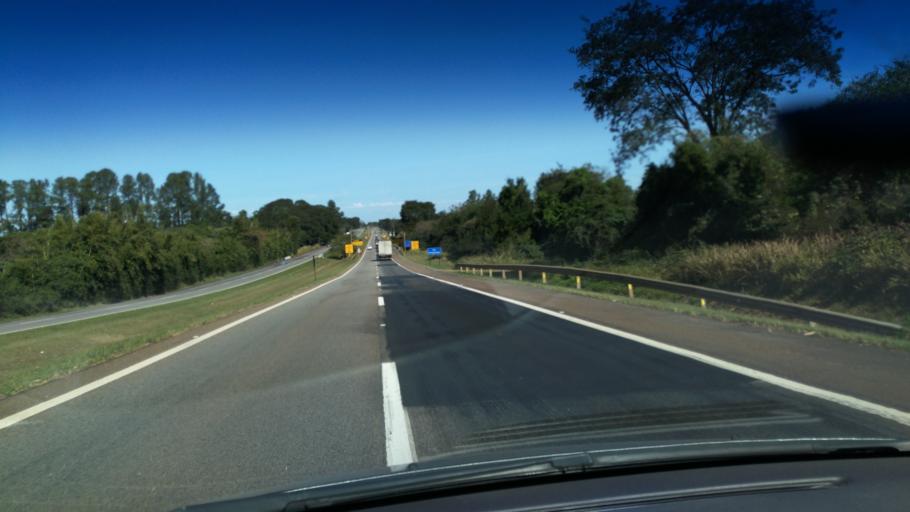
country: BR
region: Sao Paulo
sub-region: Santo Antonio De Posse
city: Santo Antonio de Posse
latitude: -22.5565
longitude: -46.9993
